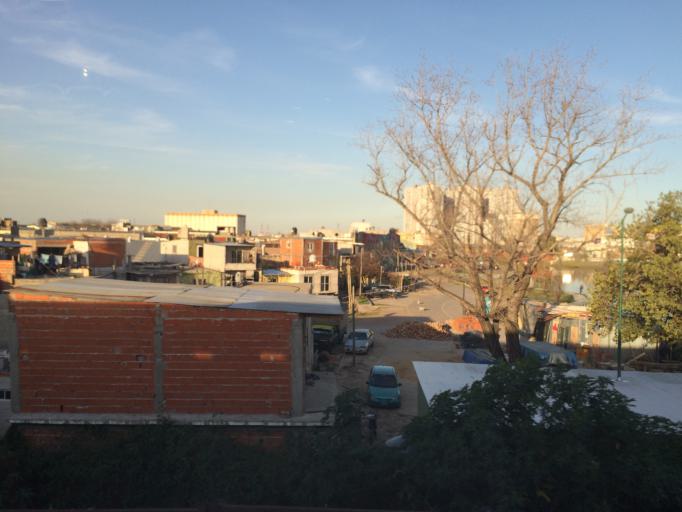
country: AR
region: Buenos Aires
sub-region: Partido de Avellaneda
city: Avellaneda
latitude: -34.6569
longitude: -58.3778
